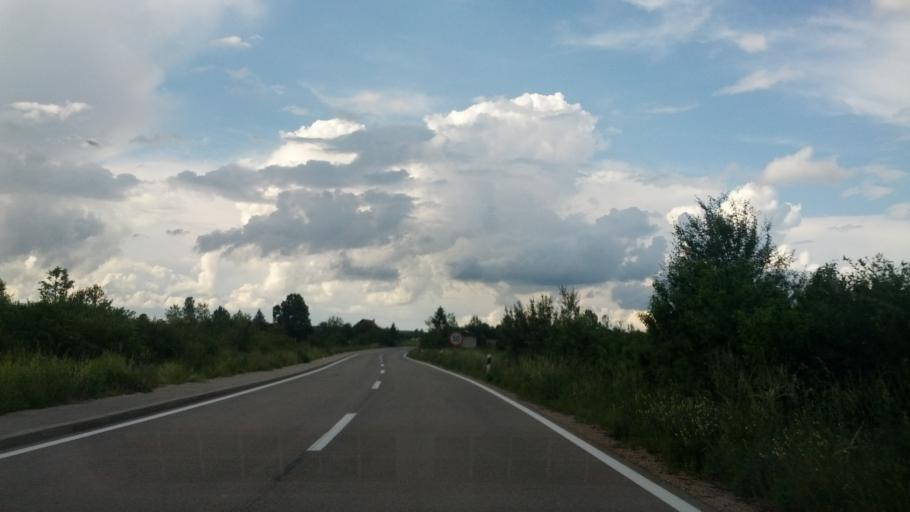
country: BA
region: Federation of Bosnia and Herzegovina
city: Izacic
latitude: 44.8958
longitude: 15.7240
